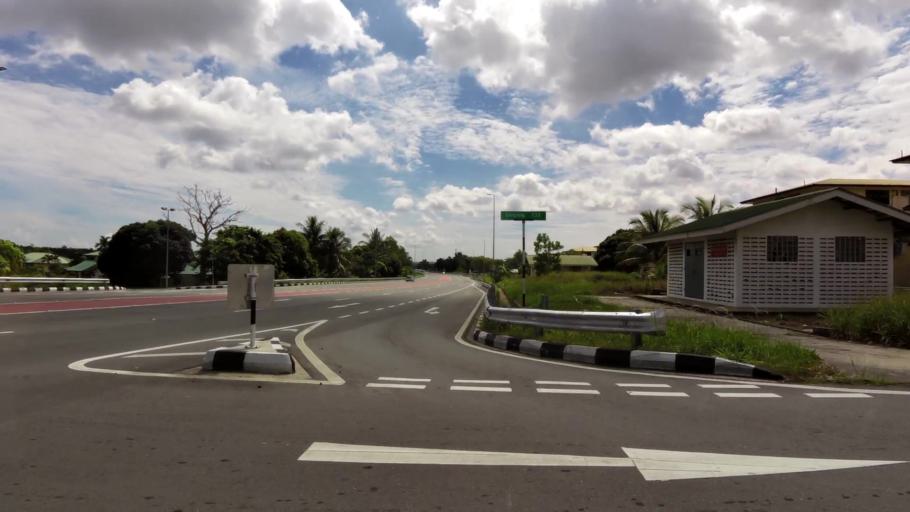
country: BN
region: Brunei and Muara
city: Bandar Seri Begawan
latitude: 4.9330
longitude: 114.8937
